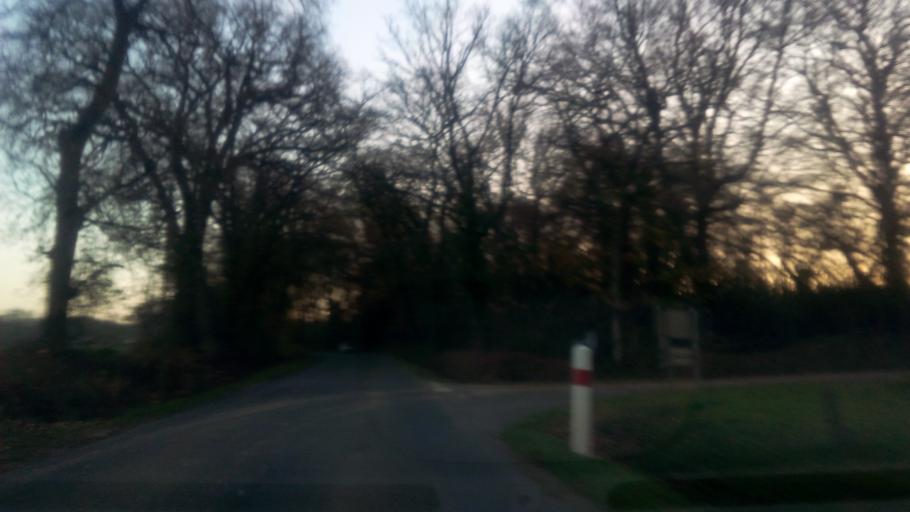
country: FR
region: Brittany
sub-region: Departement d'Ille-et-Vilaine
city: Bains-sur-Oust
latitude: 47.7131
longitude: -2.0540
